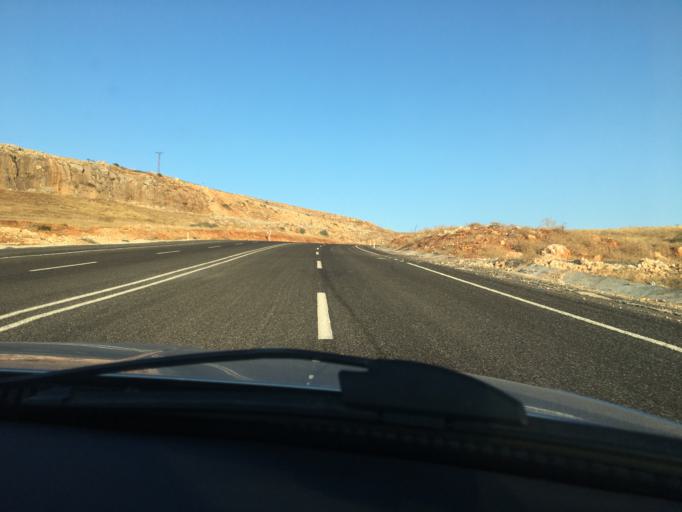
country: TR
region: Sanliurfa
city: Halfeti
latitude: 37.2388
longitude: 37.8802
